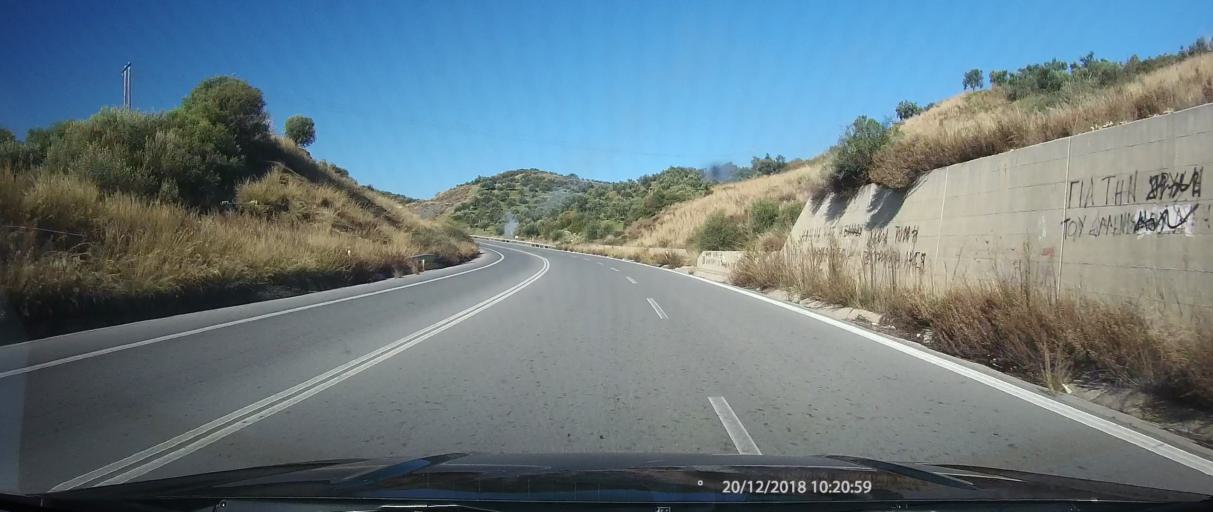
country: GR
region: Peloponnese
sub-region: Nomos Lakonias
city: Magoula
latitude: 37.1555
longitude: 22.4319
